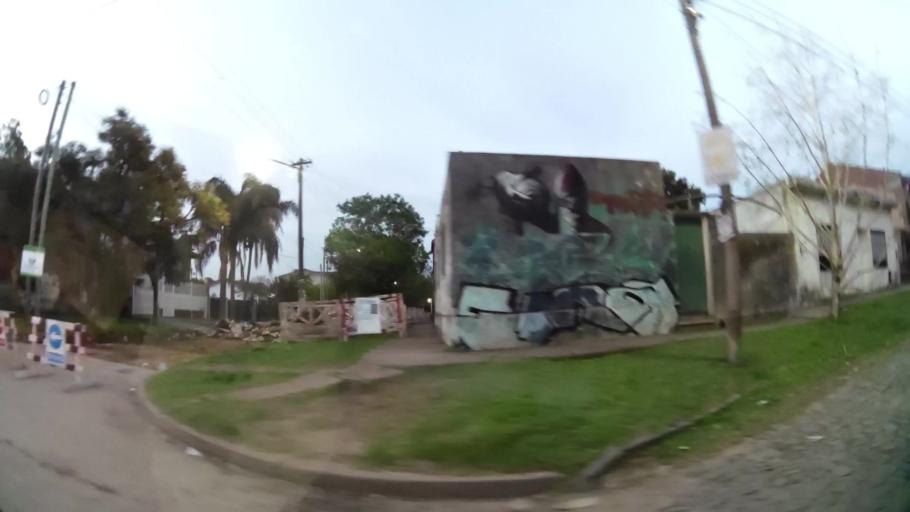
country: AR
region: Buenos Aires
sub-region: Partido de Quilmes
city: Quilmes
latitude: -34.8072
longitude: -58.2815
